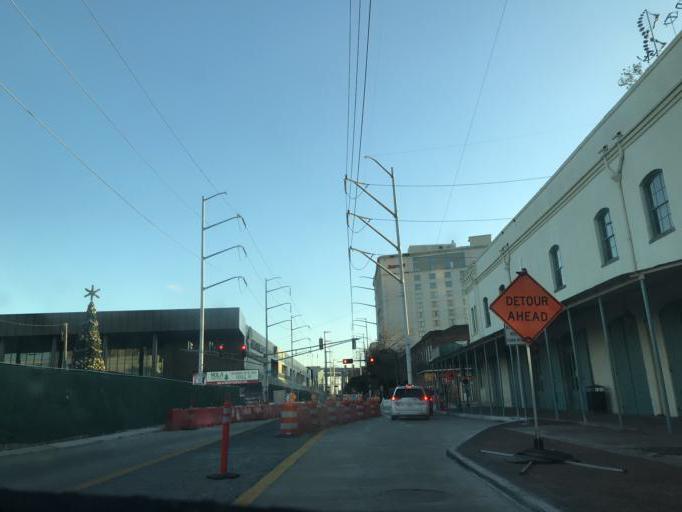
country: US
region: Louisiana
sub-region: Orleans Parish
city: New Orleans
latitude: 29.9449
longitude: -90.0647
